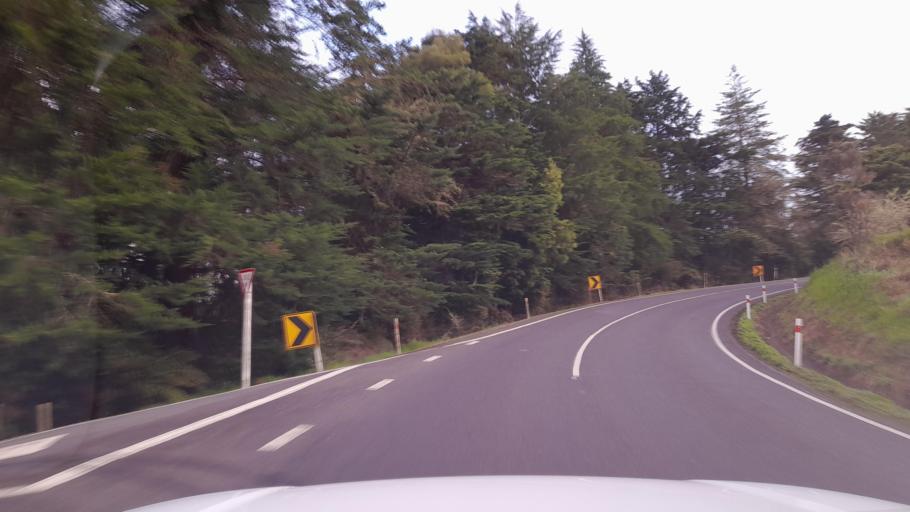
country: NZ
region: Northland
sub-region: Far North District
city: Waimate North
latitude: -35.5161
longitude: 173.8311
